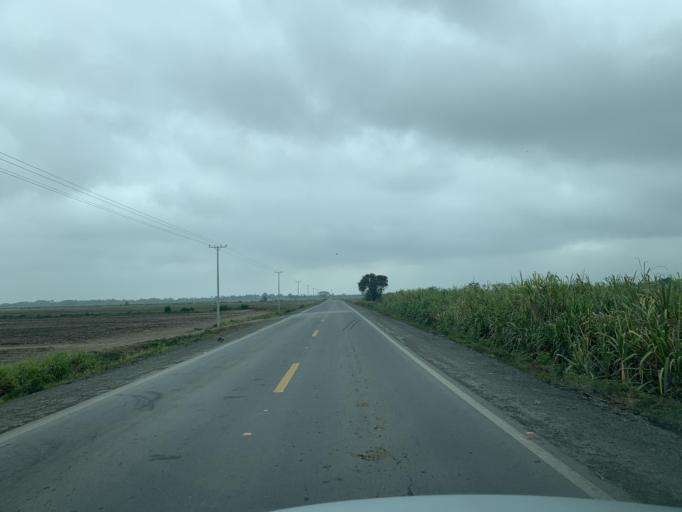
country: EC
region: Guayas
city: Coronel Marcelino Mariduena
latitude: -2.3116
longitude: -79.5117
